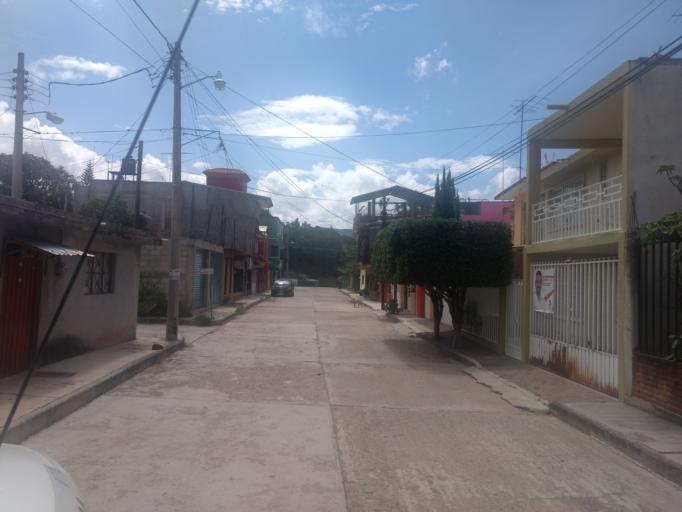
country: MX
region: Oaxaca
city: Ciudad de Huajuapam de Leon
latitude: 17.8023
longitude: -97.7752
